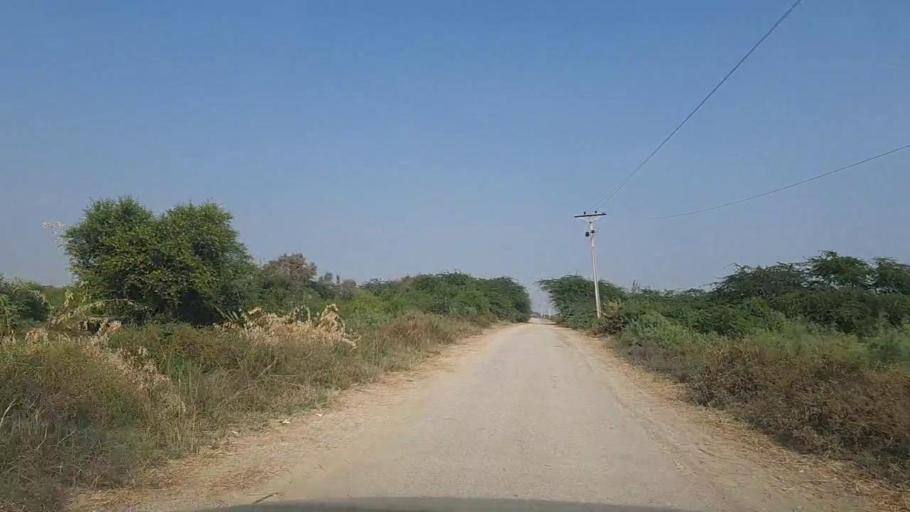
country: PK
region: Sindh
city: Thatta
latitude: 24.6024
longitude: 67.9531
